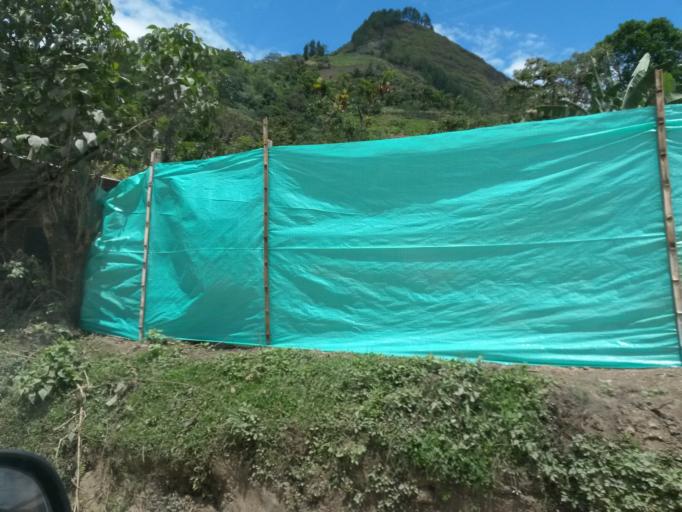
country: CO
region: Cauca
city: Inza
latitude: 2.5531
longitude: -76.0507
